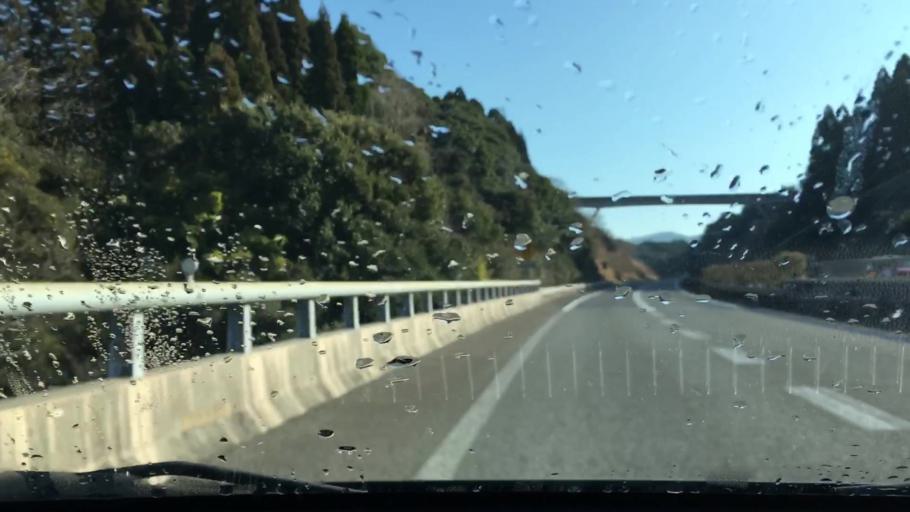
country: JP
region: Kagoshima
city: Kokubu-matsuki
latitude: 31.7430
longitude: 130.7998
